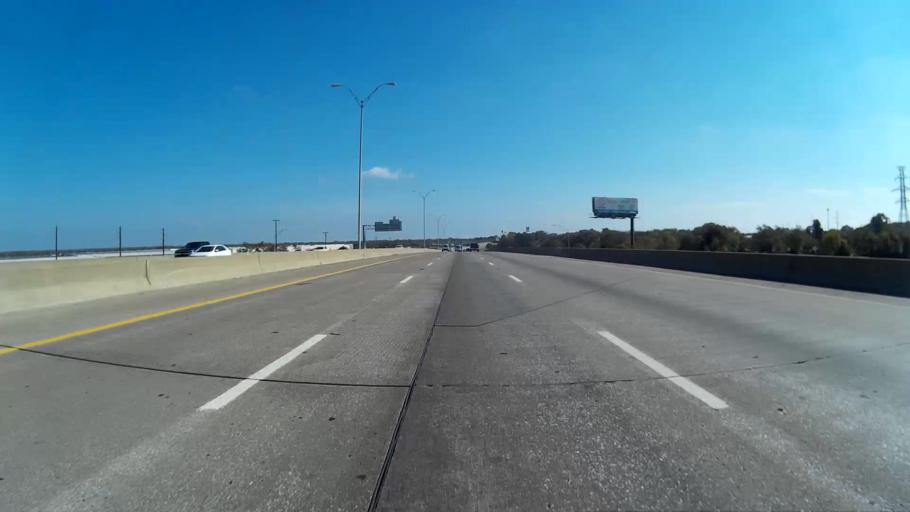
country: US
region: Texas
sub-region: Dallas County
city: Hutchins
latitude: 32.6553
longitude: -96.7161
